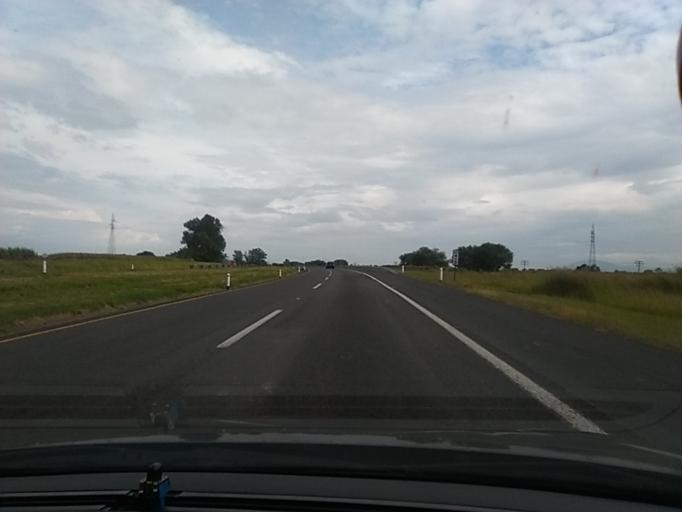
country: MX
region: Jalisco
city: Jamay
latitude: 20.3508
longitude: -102.6336
